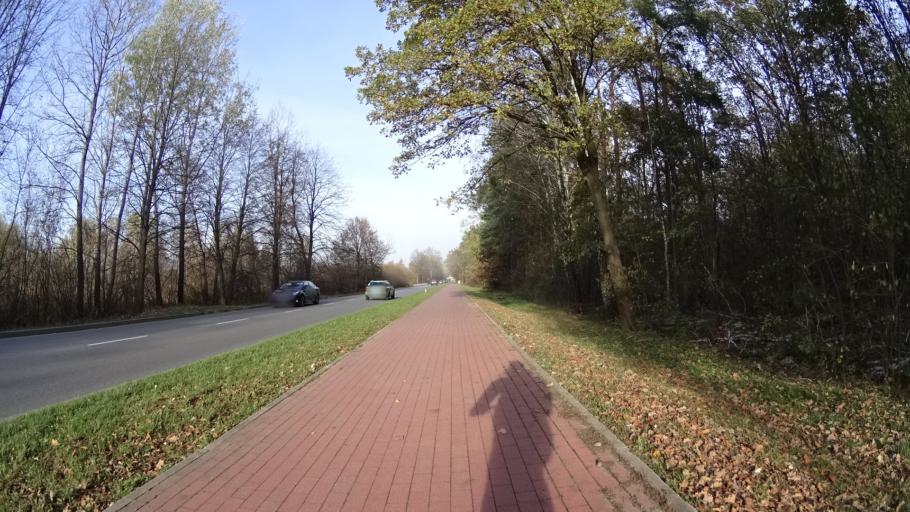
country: PL
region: Masovian Voivodeship
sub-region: Powiat warszawski zachodni
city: Babice
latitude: 52.2672
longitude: 20.8591
